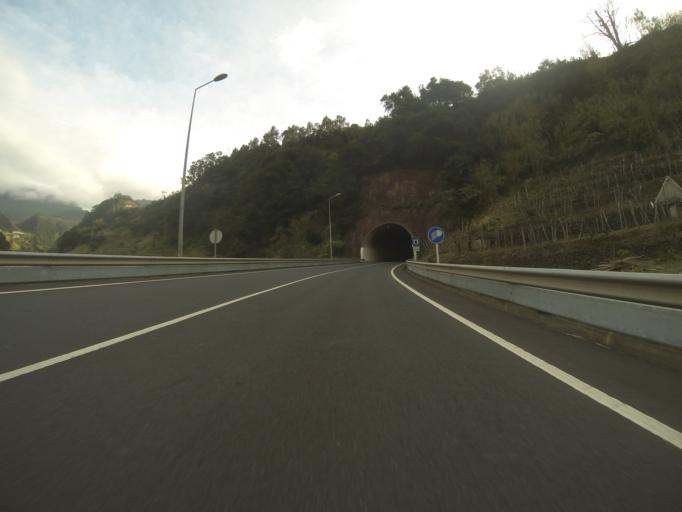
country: PT
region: Madeira
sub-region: Sao Vicente
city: Sao Vicente
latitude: 32.7852
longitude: -17.0312
